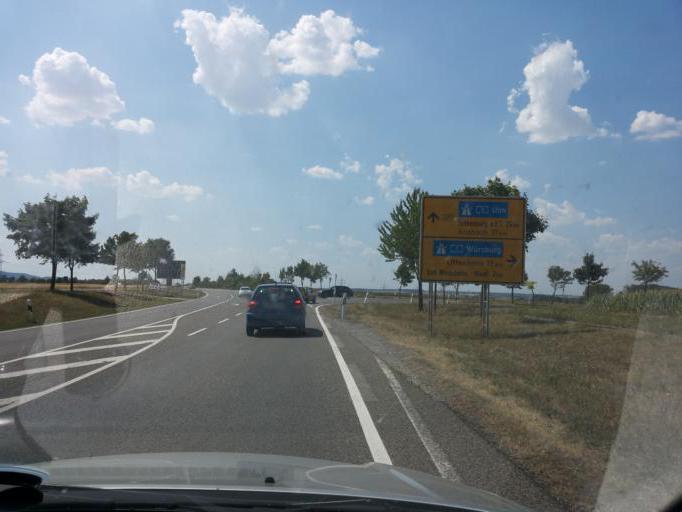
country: DE
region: Bavaria
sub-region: Regierungsbezirk Mittelfranken
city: Bad Windsheim
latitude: 49.4904
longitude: 10.3955
